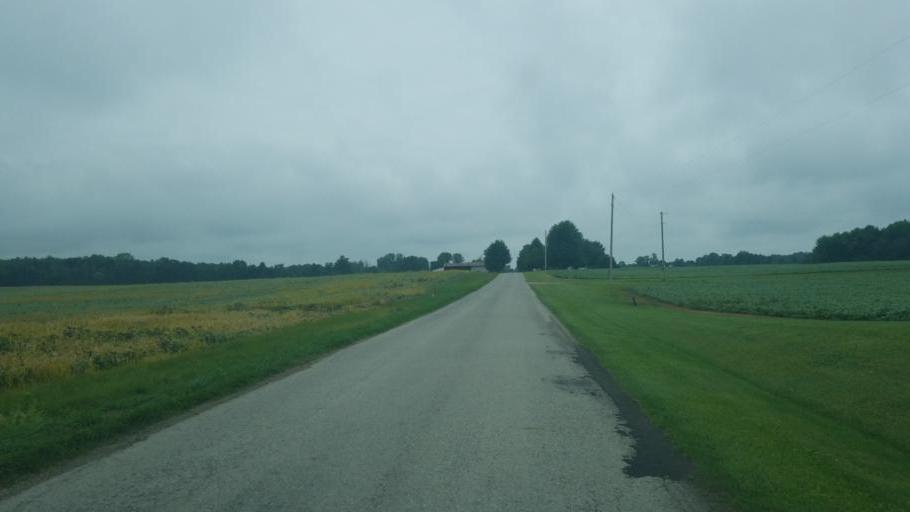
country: US
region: Ohio
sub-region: Knox County
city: Centerburg
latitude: 40.4090
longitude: -82.7569
